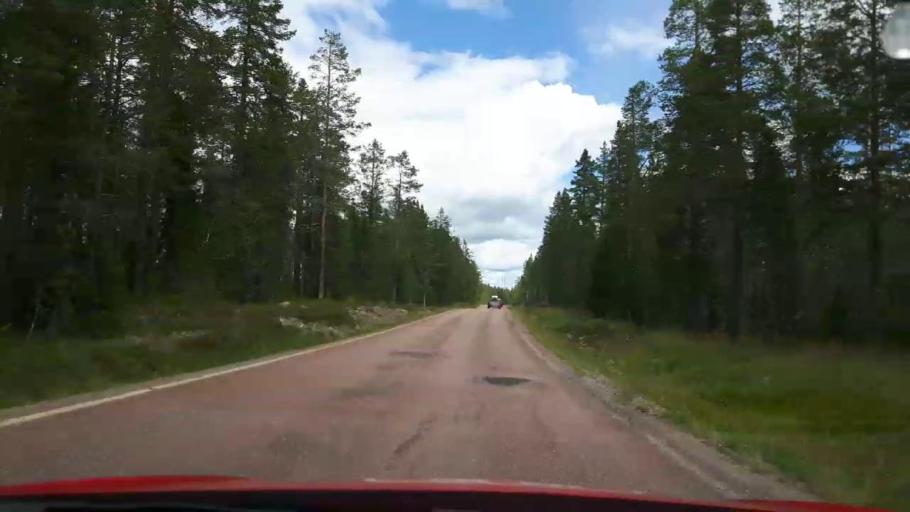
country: NO
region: Hedmark
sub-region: Trysil
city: Innbygda
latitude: 61.9012
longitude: 12.9910
